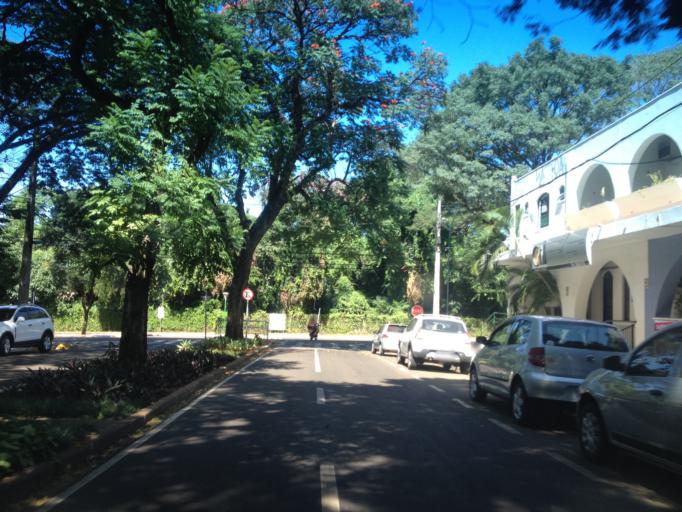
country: BR
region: Parana
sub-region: Maringa
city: Maringa
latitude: -23.4260
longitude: -51.9454
